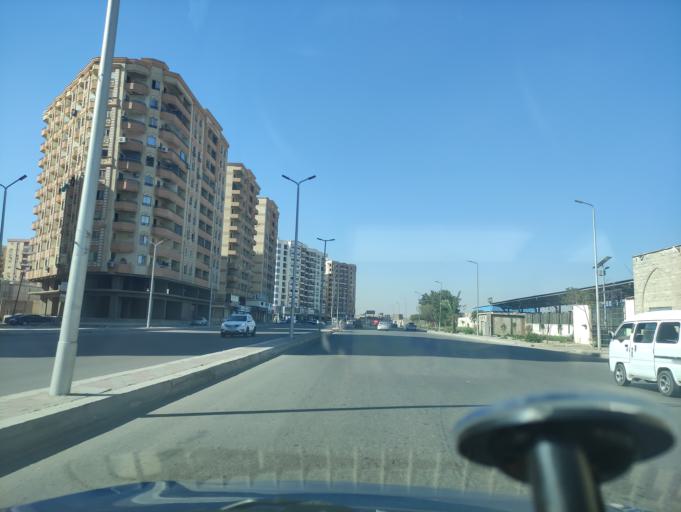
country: EG
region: Al Jizah
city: Al Jizah
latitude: 30.0041
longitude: 31.2447
